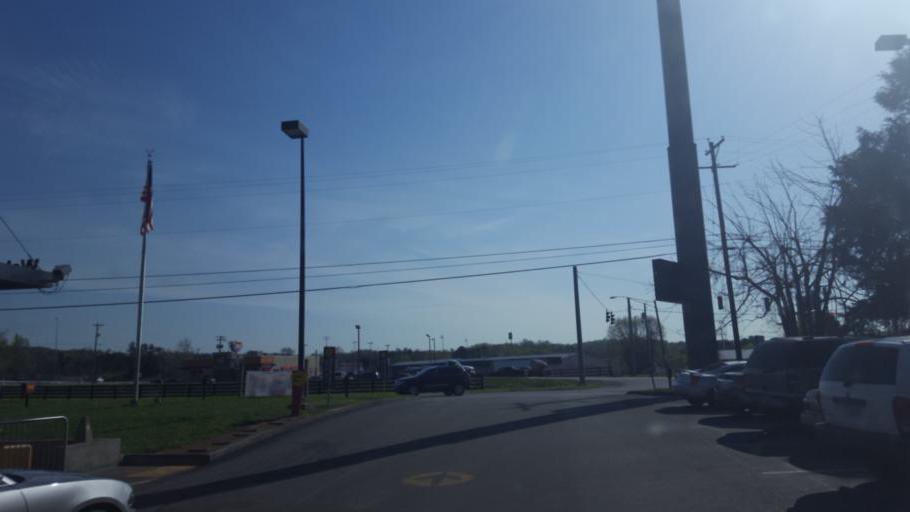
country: US
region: Kentucky
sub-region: Hart County
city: Munfordville
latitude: 37.2887
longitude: -85.9030
